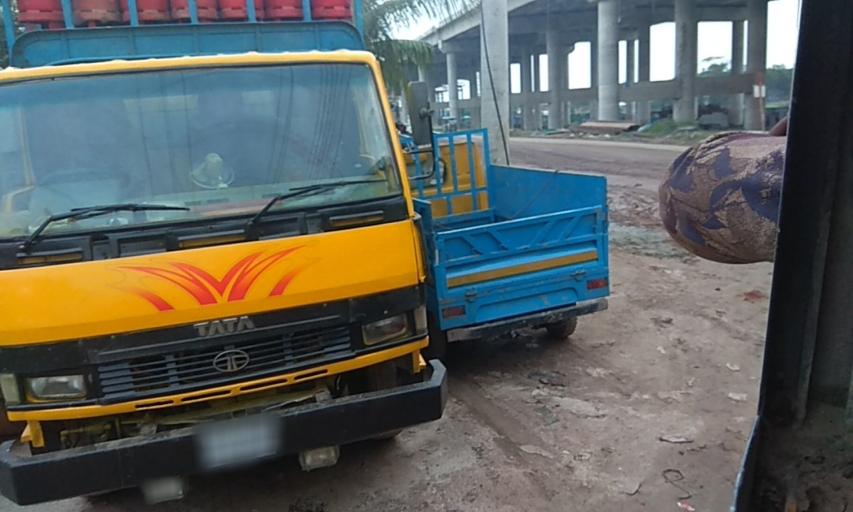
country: BD
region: Dhaka
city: Char Bhadrasan
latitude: 23.3857
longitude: 89.9947
